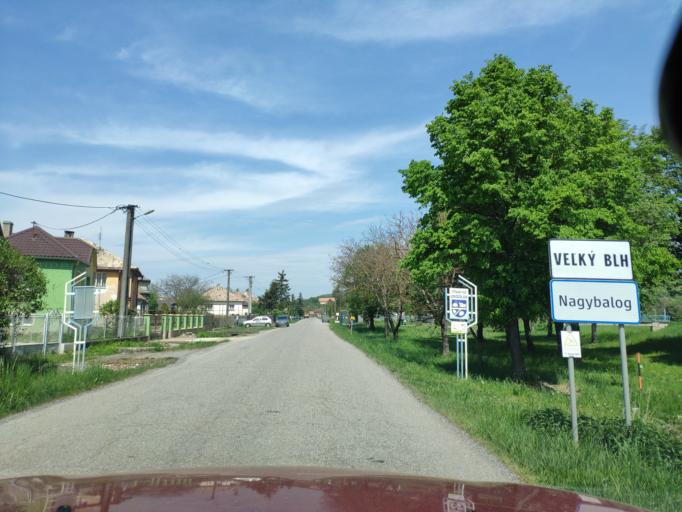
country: SK
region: Banskobystricky
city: Rimavska Sobota
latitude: 48.4402
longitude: 20.1150
